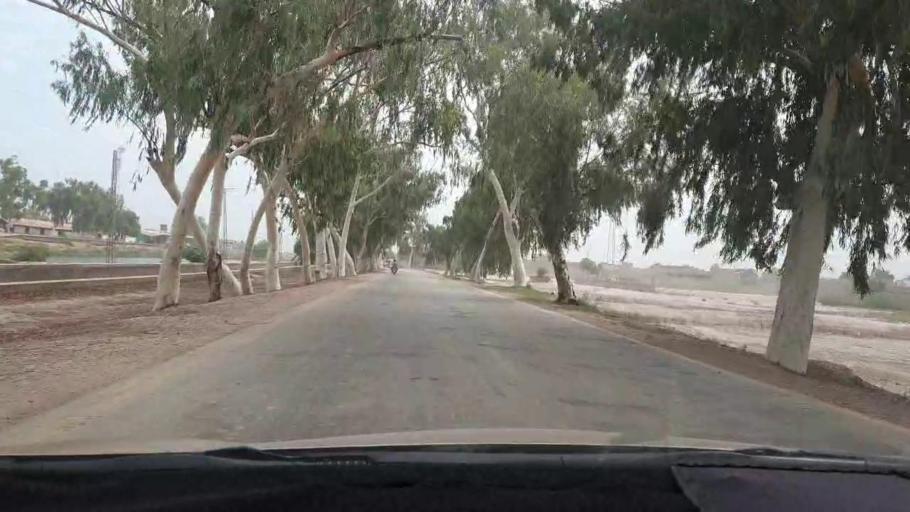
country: PK
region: Sindh
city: Naudero
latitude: 27.6684
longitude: 68.3528
